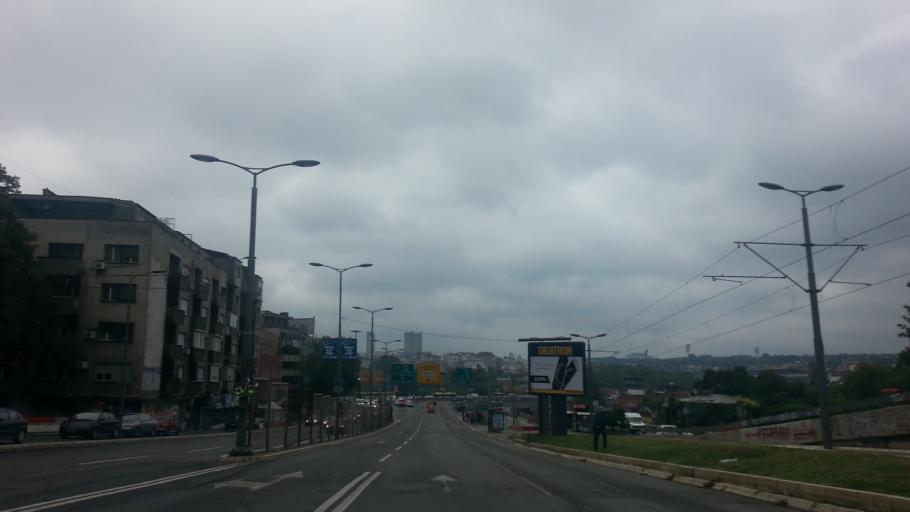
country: RS
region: Central Serbia
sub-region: Belgrade
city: Vracar
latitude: 44.7938
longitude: 20.4660
